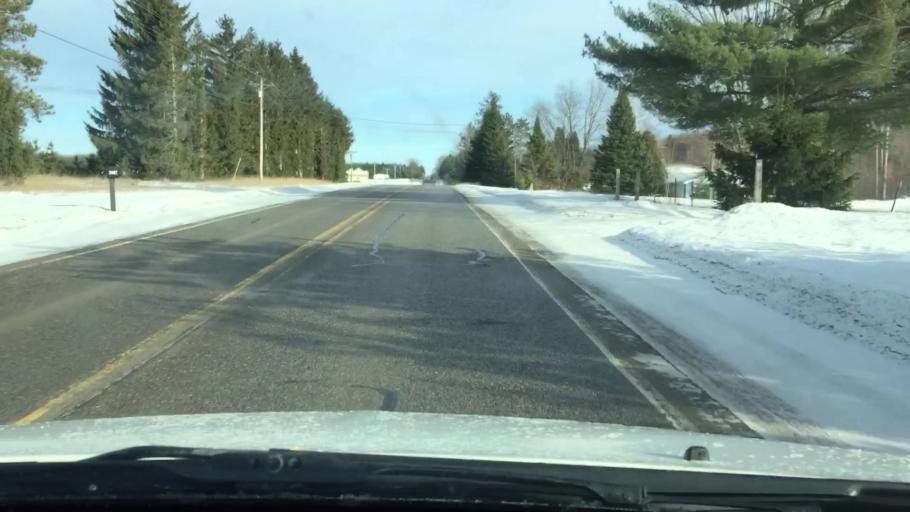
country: US
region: Michigan
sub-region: Kalkaska County
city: Kalkaska
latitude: 44.6408
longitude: -85.2492
